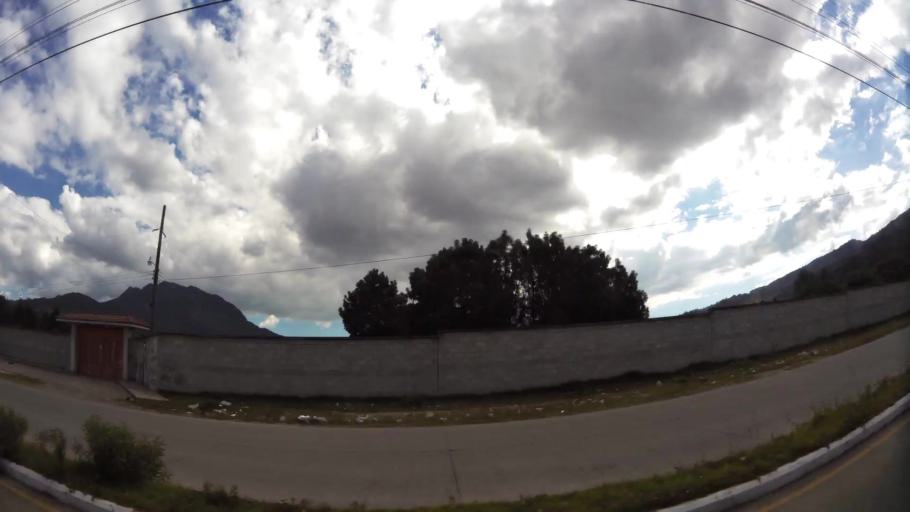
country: GT
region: Quetzaltenango
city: Quetzaltenango
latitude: 14.8322
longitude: -91.5441
